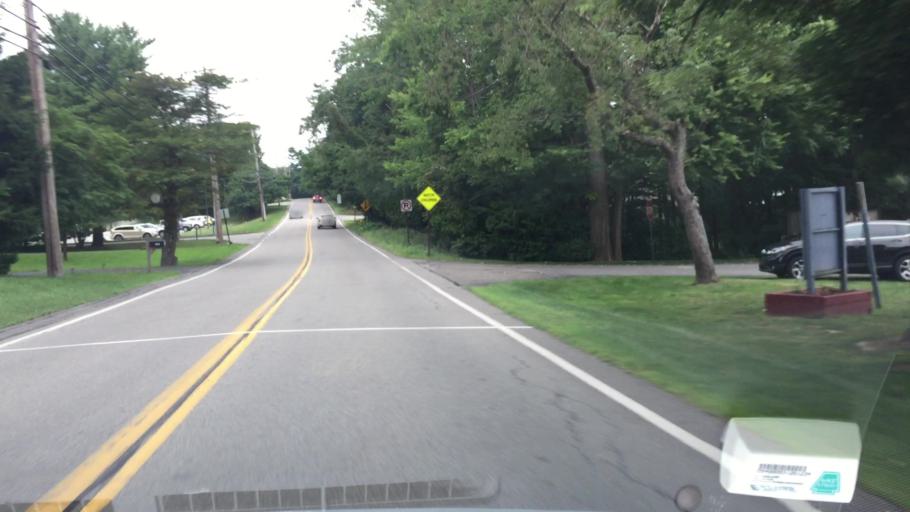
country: US
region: Pennsylvania
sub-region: Allegheny County
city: Allison Park
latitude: 40.5728
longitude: -79.9268
